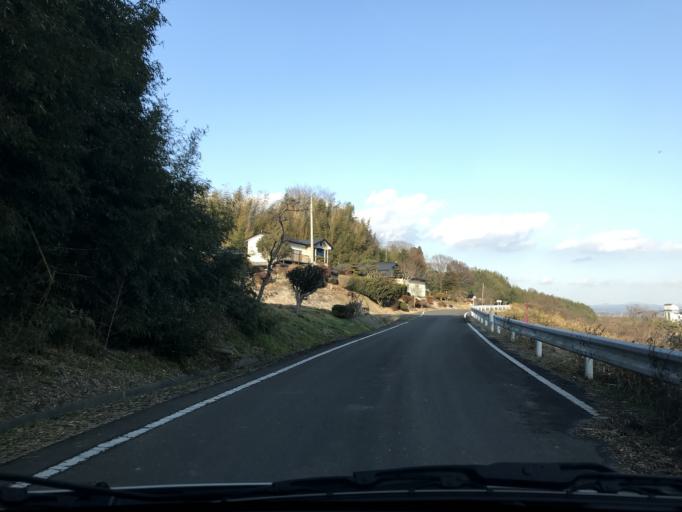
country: JP
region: Miyagi
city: Wakuya
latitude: 38.7079
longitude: 141.1396
